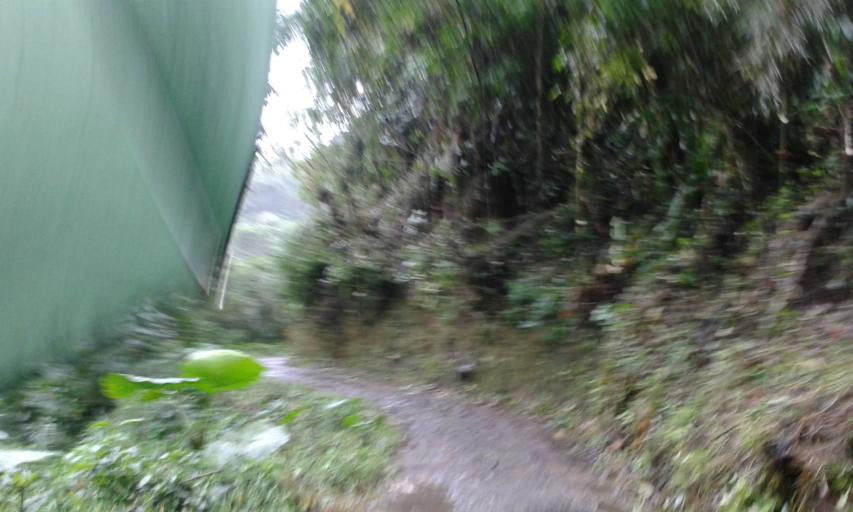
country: CR
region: San Jose
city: Ipis
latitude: 10.0309
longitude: -83.9328
